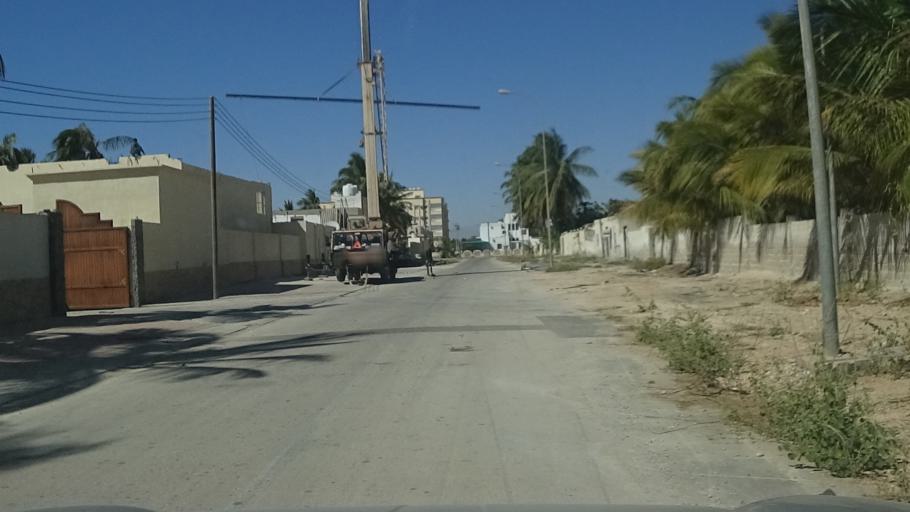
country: OM
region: Zufar
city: Salalah
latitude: 17.0288
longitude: 54.1622
